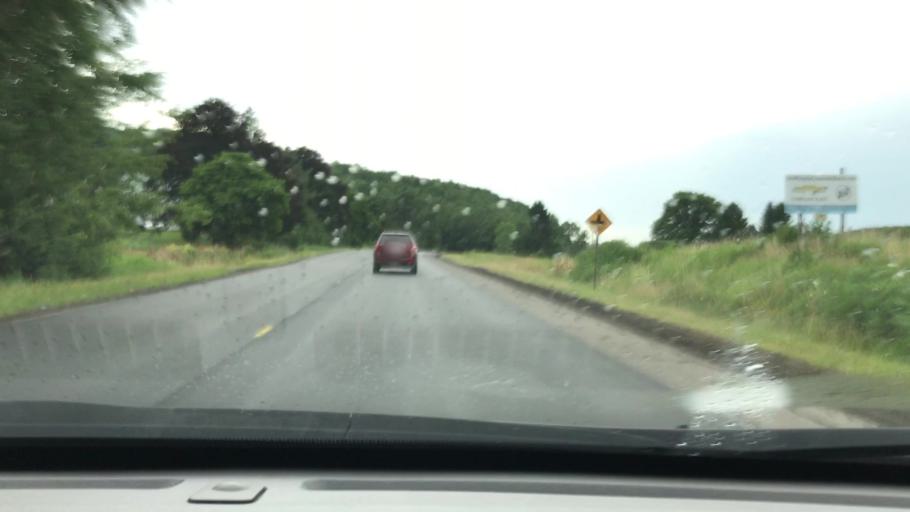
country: US
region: New York
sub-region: Erie County
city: Springville
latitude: 42.3620
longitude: -78.6547
